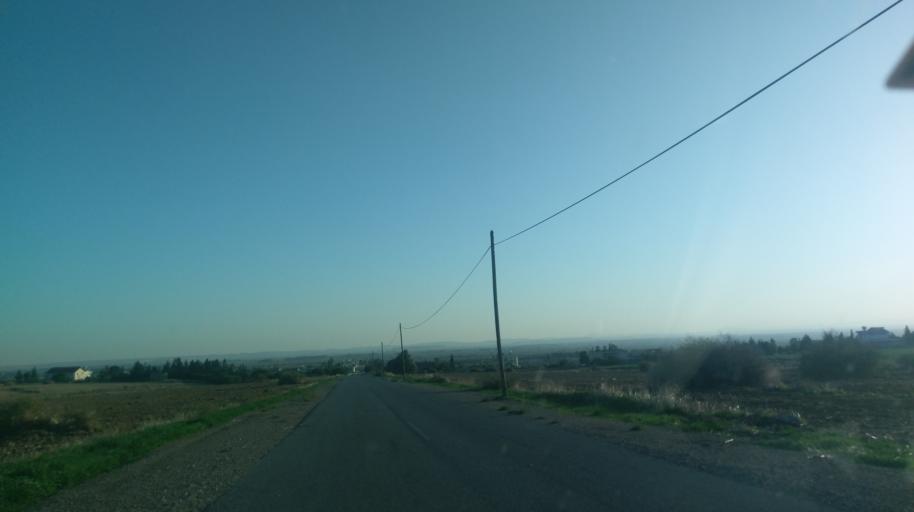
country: CY
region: Larnaka
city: Athienou
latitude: 35.2373
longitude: 33.5550
